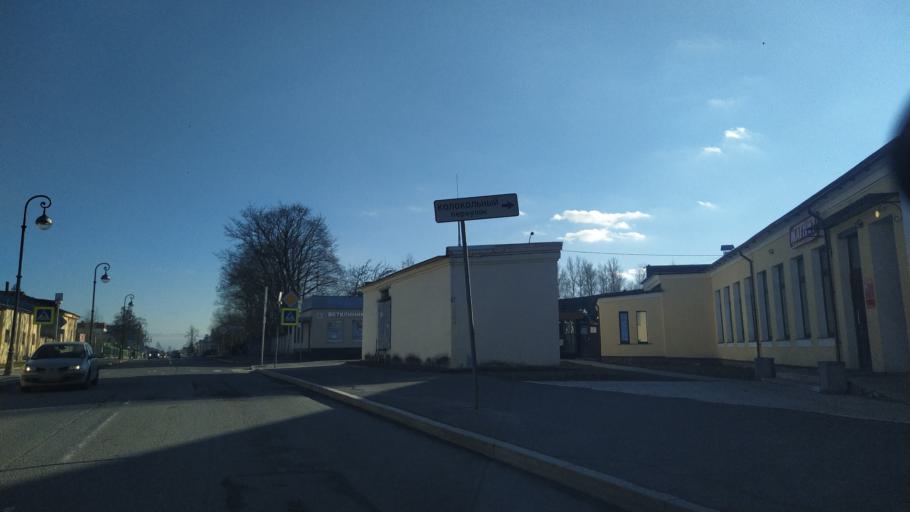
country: RU
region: St.-Petersburg
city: Pushkin
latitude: 59.7069
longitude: 30.3906
